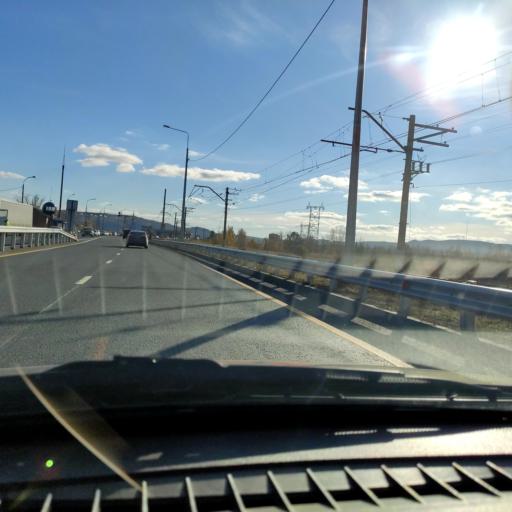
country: RU
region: Samara
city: Zhigulevsk
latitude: 53.4688
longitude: 49.5040
